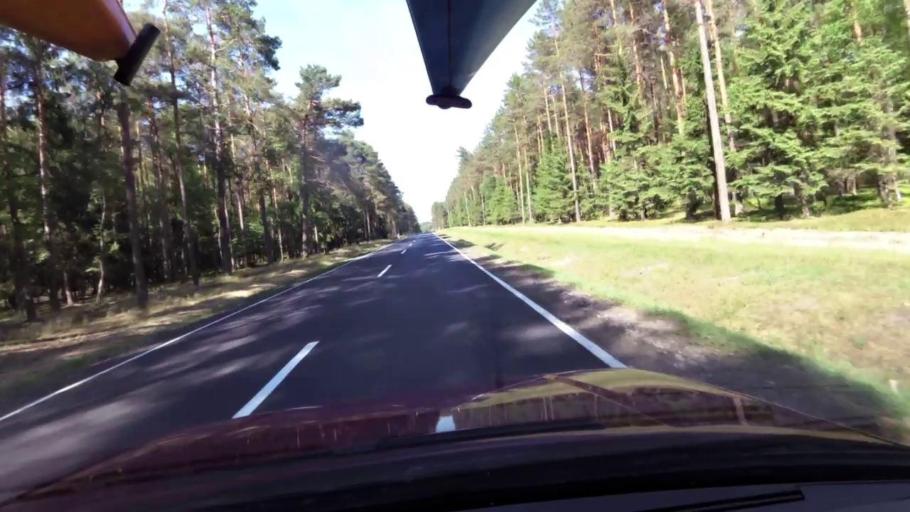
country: PL
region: Pomeranian Voivodeship
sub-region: Powiat bytowski
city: Trzebielino
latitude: 54.1381
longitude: 17.0231
